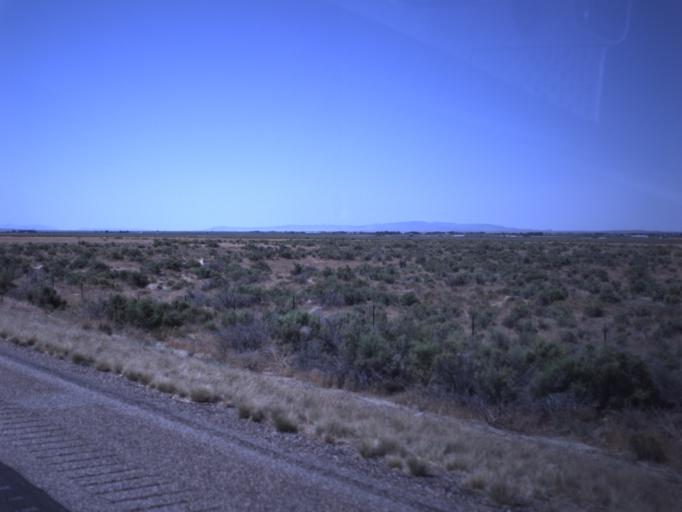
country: US
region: Utah
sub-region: Millard County
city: Delta
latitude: 39.3624
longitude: -112.4965
